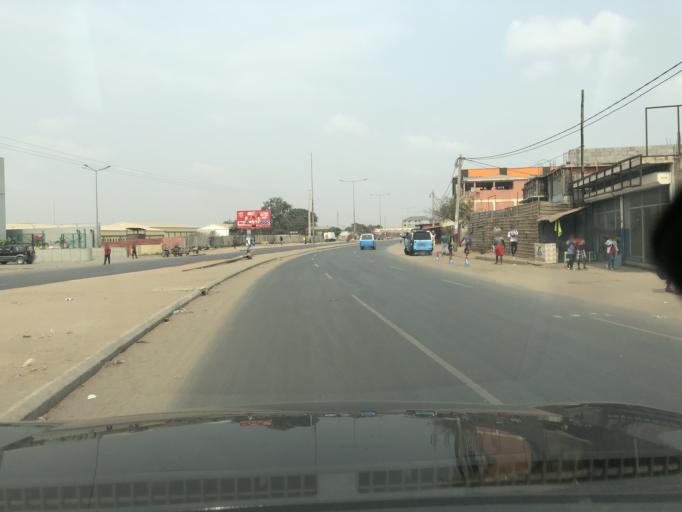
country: AO
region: Luanda
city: Luanda
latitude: -8.7989
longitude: 13.3142
